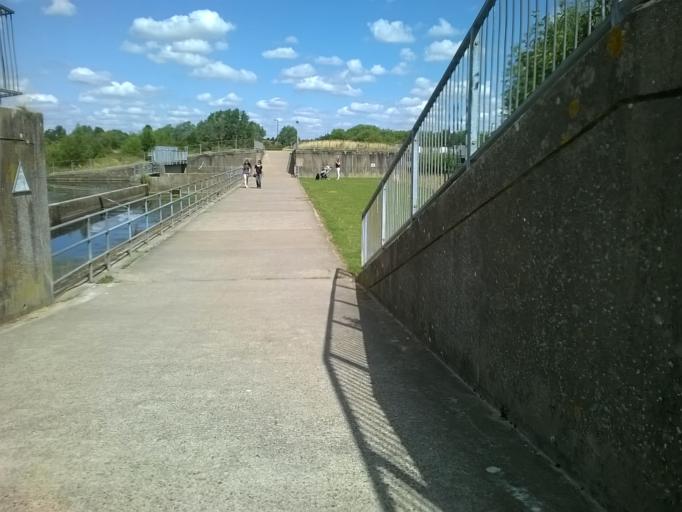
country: GB
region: England
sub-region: Milton Keynes
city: Broughton
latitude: 52.0576
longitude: -0.7148
